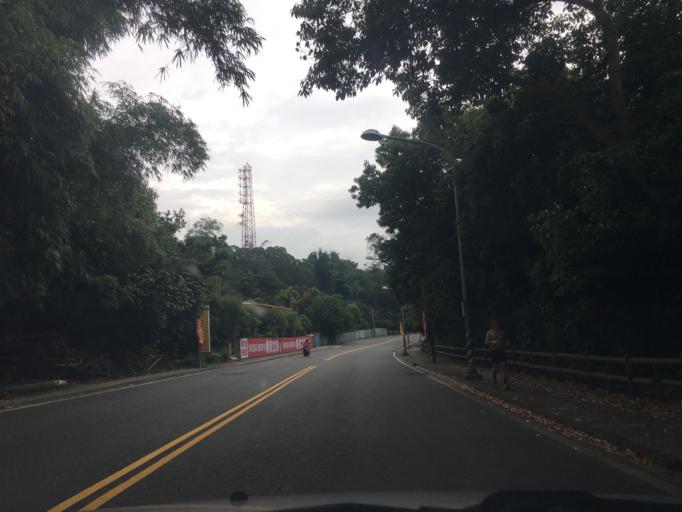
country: TW
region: Taiwan
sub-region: Changhua
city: Chang-hua
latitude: 24.0620
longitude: 120.5727
